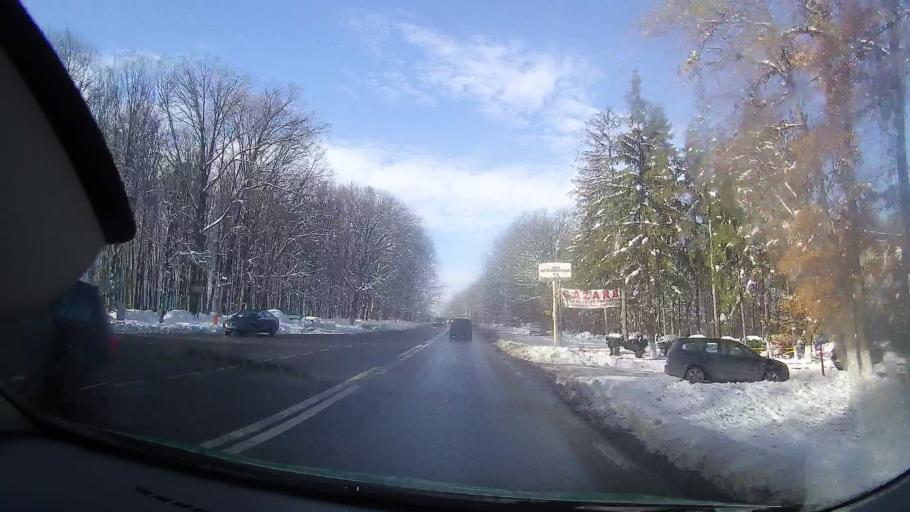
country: RO
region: Iasi
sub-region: Comuna Motca
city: Motca
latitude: 47.2540
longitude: 26.6238
